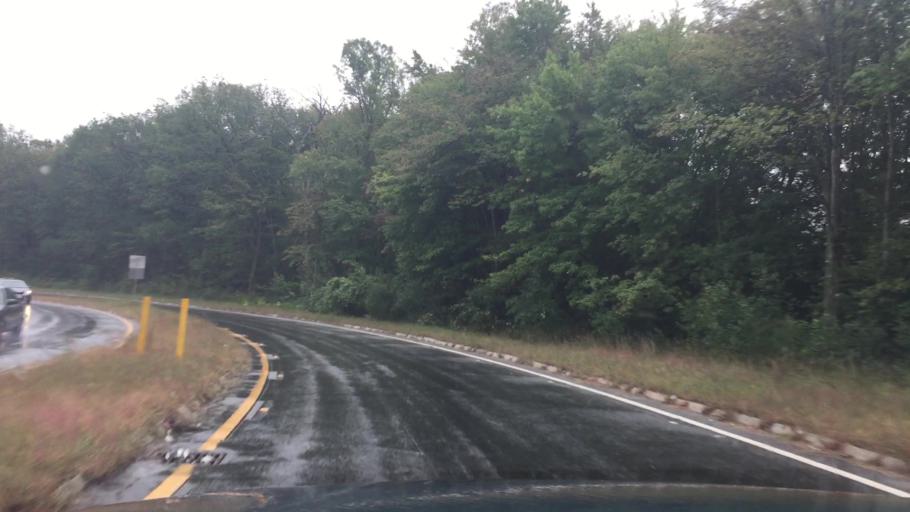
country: US
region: Massachusetts
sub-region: Norfolk County
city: Bellingham
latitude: 42.1129
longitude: -71.4677
